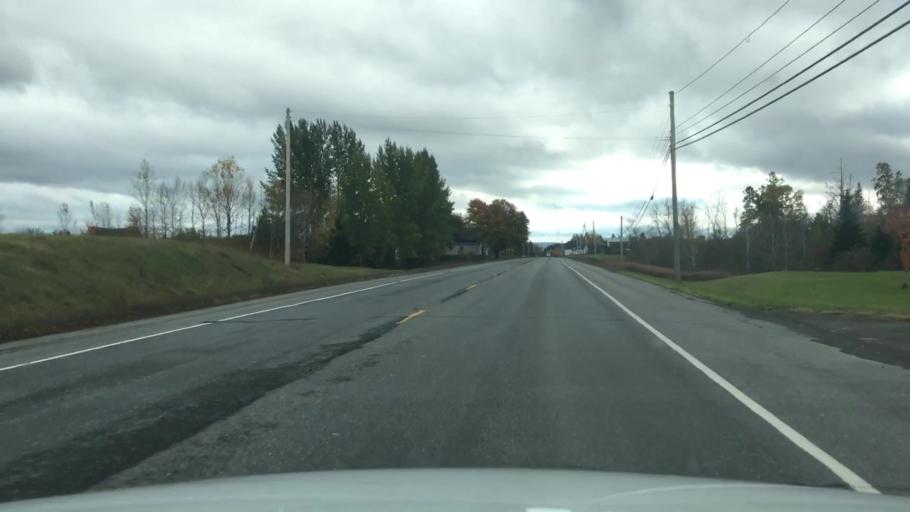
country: US
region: Maine
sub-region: Aroostook County
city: Houlton
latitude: 46.1828
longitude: -67.8411
